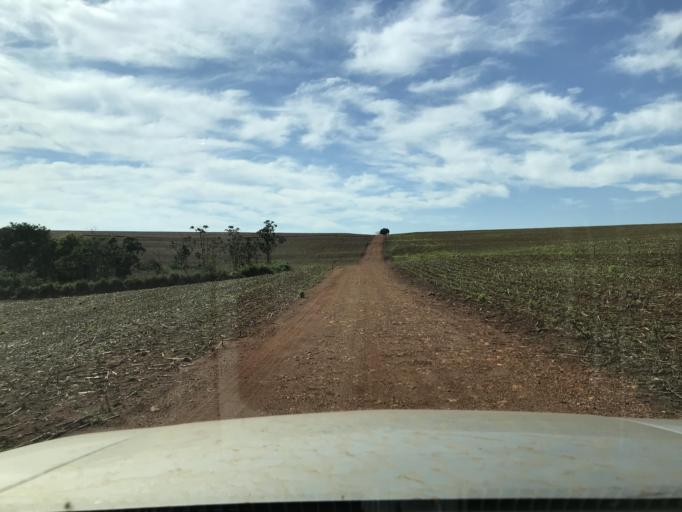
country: BR
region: Parana
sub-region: Palotina
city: Palotina
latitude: -24.1839
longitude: -53.8377
